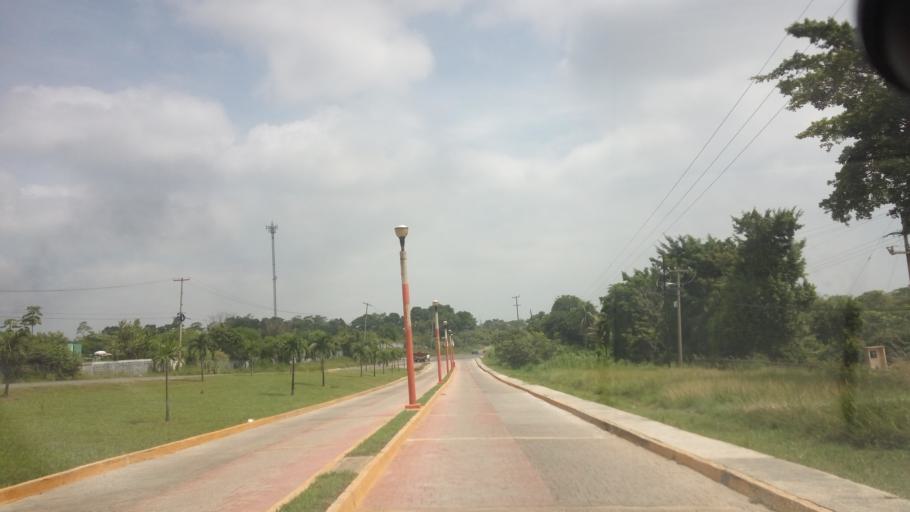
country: MX
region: Chiapas
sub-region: Reforma
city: El Carmen (El Limon)
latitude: 17.8738
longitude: -93.1508
